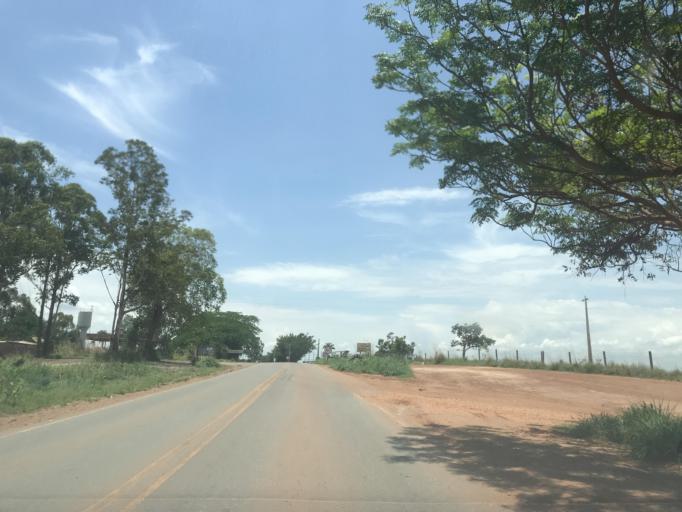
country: BR
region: Goias
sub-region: Vianopolis
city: Vianopolis
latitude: -16.5850
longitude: -48.3456
